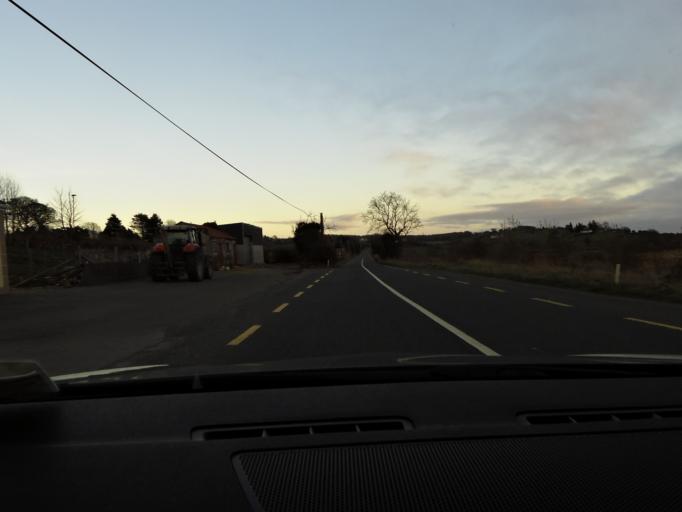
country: IE
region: Connaught
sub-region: Sligo
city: Ballymote
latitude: 53.9789
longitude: -8.4582
